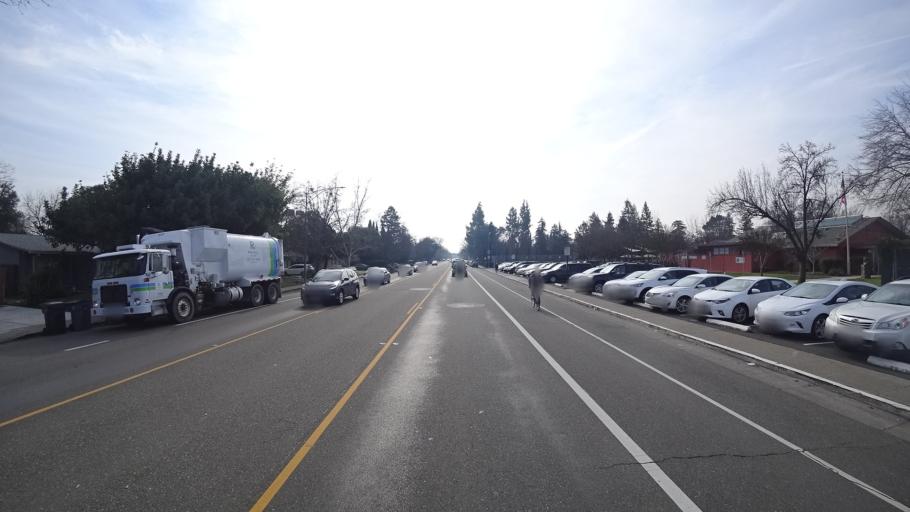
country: US
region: California
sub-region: Yolo County
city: Davis
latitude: 38.5544
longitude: -121.7587
